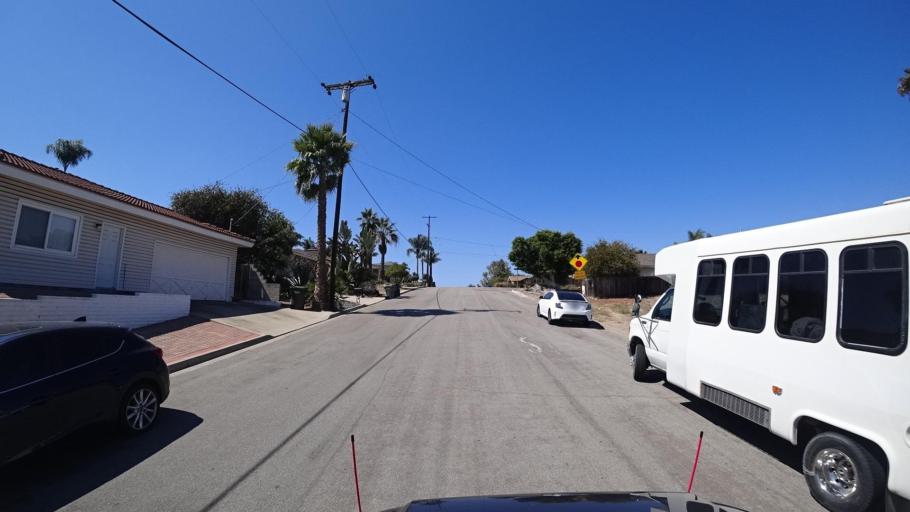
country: US
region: California
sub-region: San Diego County
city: Lake San Marcos
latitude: 33.1283
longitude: -117.2132
